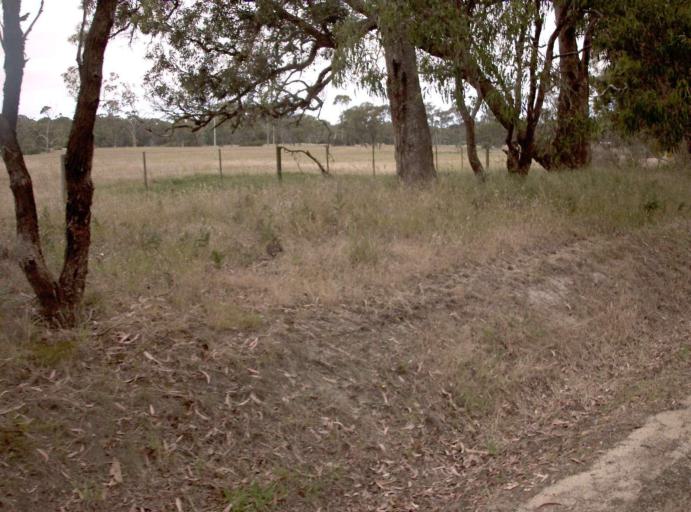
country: AU
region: Victoria
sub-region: Latrobe
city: Traralgon
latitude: -38.5209
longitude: 146.8593
